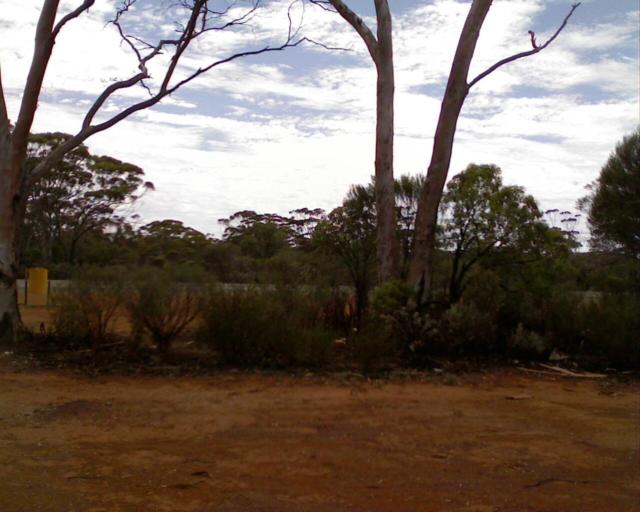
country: AU
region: Western Australia
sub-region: Kalgoorlie/Boulder
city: Stoneville
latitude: -31.1094
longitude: 121.6175
